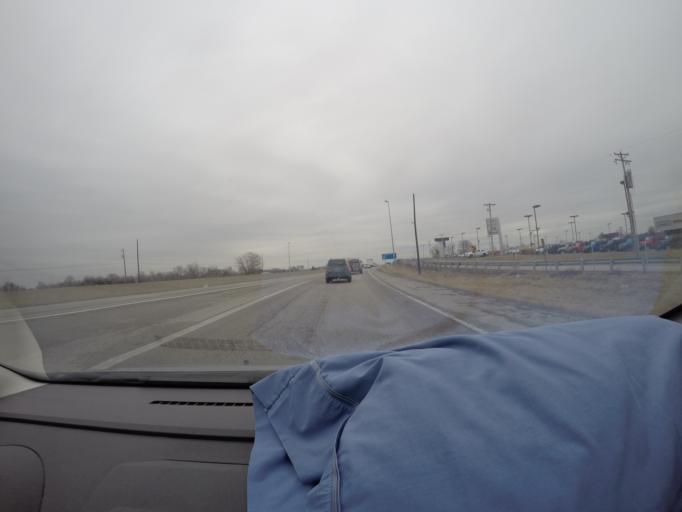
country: US
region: Missouri
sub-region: Saint Charles County
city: Wentzville
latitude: 38.8060
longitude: -90.8265
